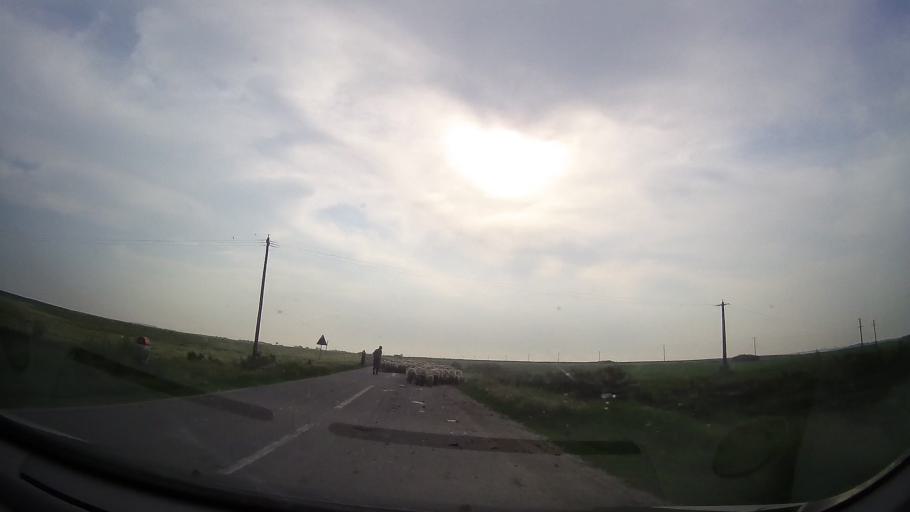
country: RO
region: Timis
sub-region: Comuna Foeni
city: Foeni
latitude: 45.4911
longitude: 20.8431
